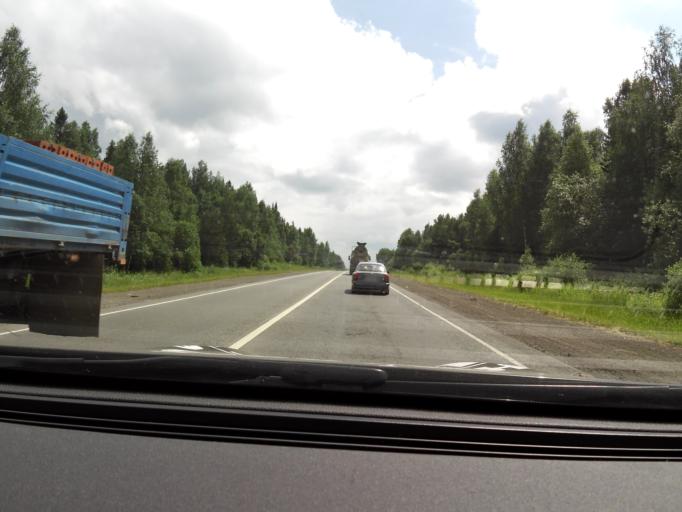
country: RU
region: Perm
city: Kungur
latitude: 57.3217
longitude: 56.9640
